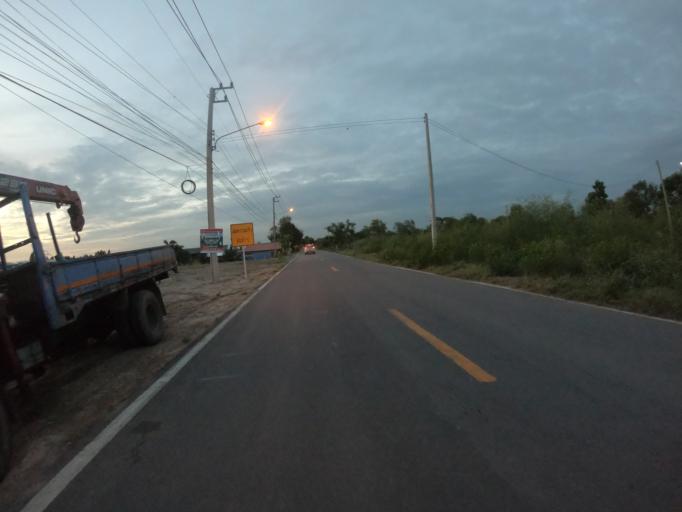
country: TH
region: Pathum Thani
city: Ban Rangsit
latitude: 14.0391
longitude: 100.8008
